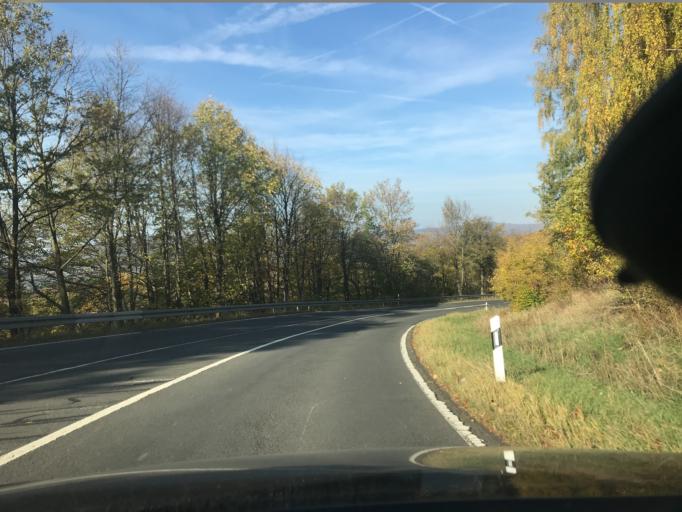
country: DE
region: Hesse
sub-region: Regierungsbezirk Kassel
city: Grossalmerode
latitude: 51.2088
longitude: 9.8274
